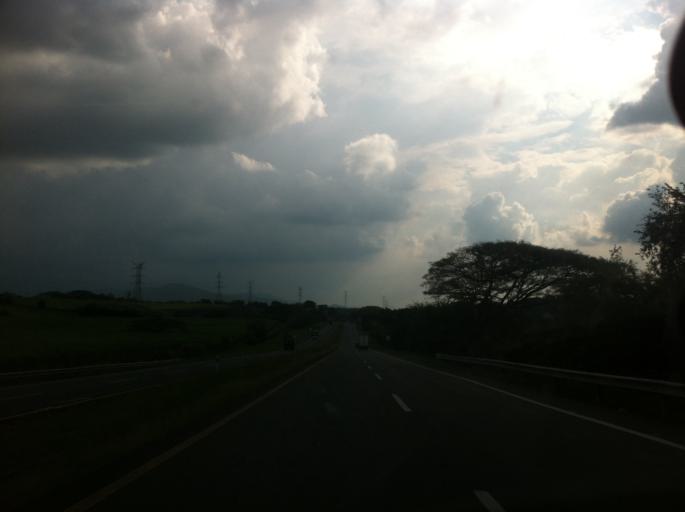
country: CO
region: Valle del Cauca
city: Tulua
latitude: 4.0775
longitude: -76.1760
